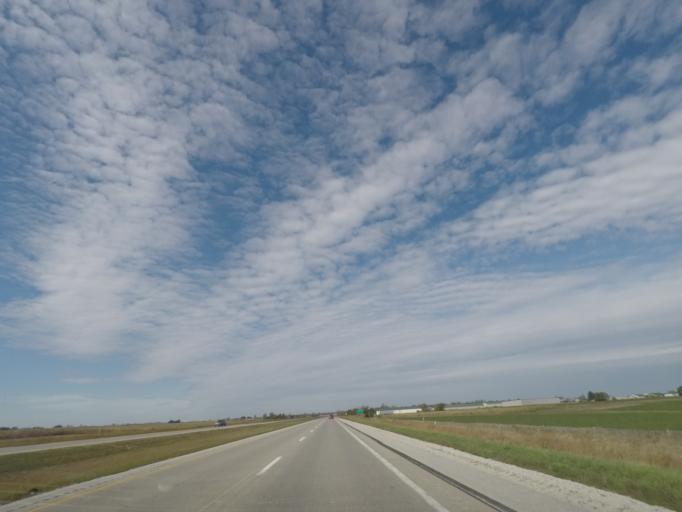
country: US
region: Iowa
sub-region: Story County
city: Ames
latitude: 42.0175
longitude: -93.7085
